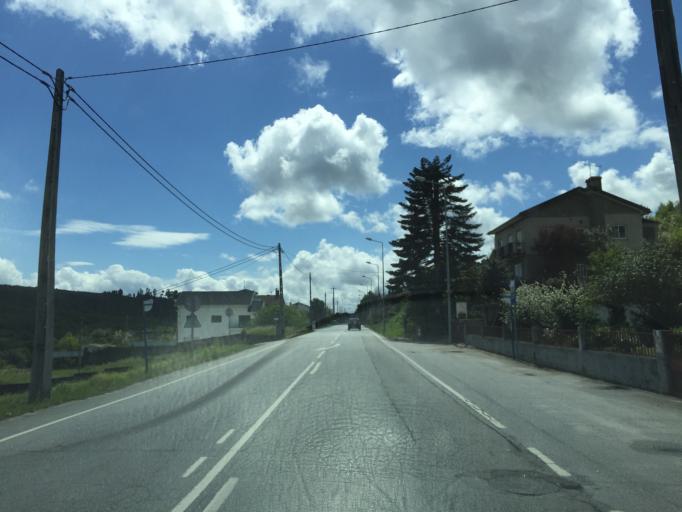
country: PT
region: Viseu
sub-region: Viseu
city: Viseu
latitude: 40.6542
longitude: -7.9455
